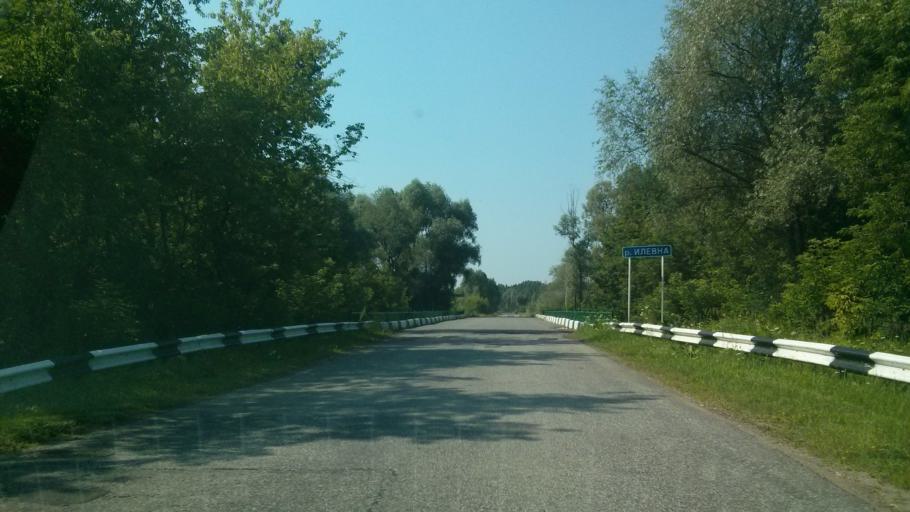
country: RU
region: Vladimir
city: Murom
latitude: 55.5015
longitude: 41.9826
